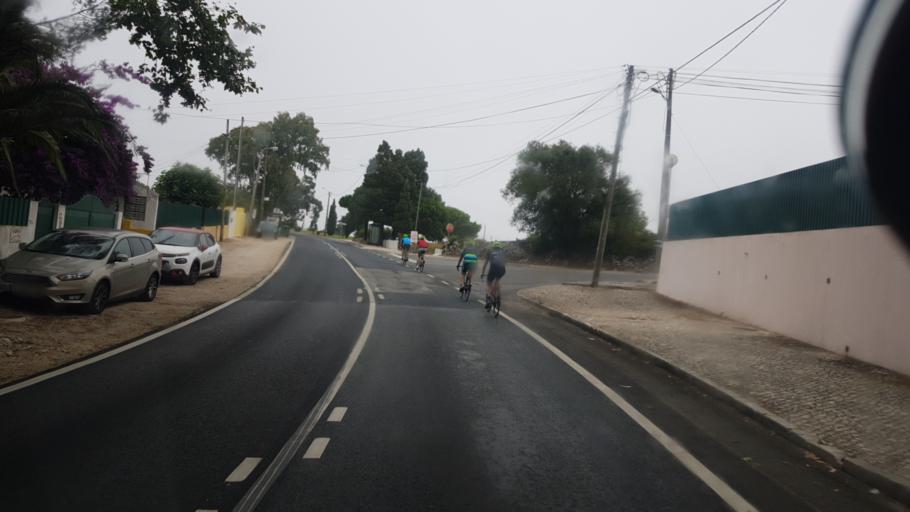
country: PT
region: Lisbon
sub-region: Sintra
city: Sintra
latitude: 38.8170
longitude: -9.3671
